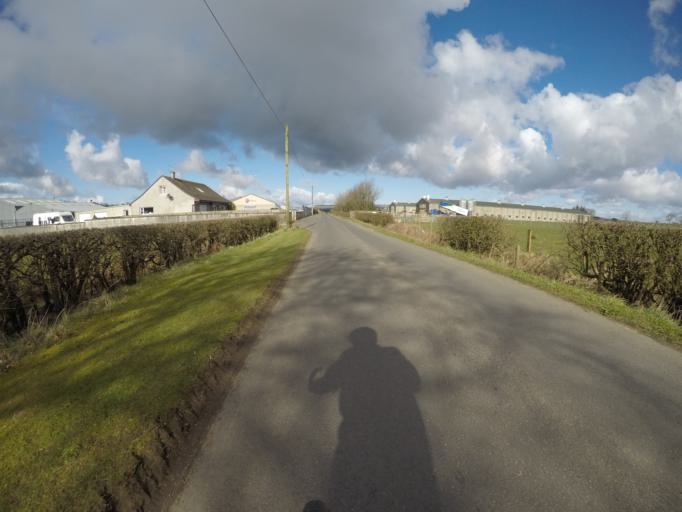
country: GB
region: Scotland
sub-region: North Ayrshire
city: Kilwinning
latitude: 55.6864
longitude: -4.6576
